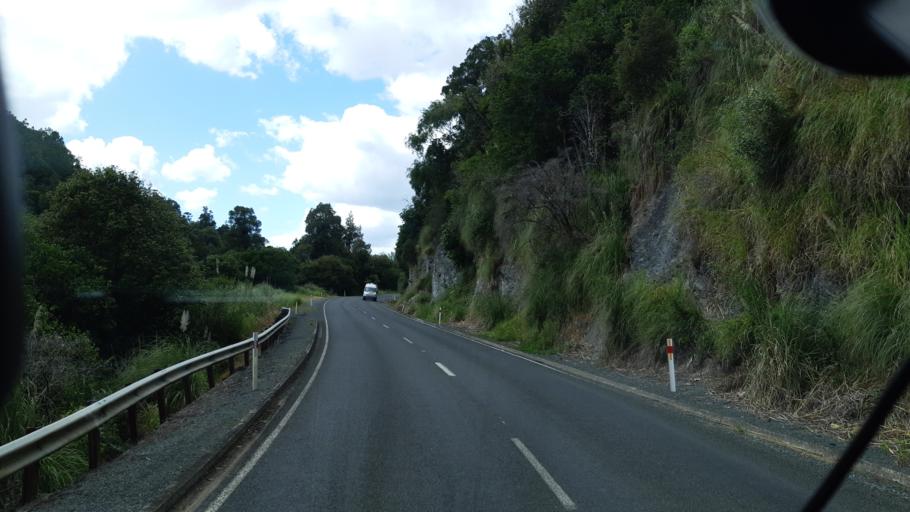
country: NZ
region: Northland
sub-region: Far North District
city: Taipa
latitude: -35.2493
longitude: 173.5308
